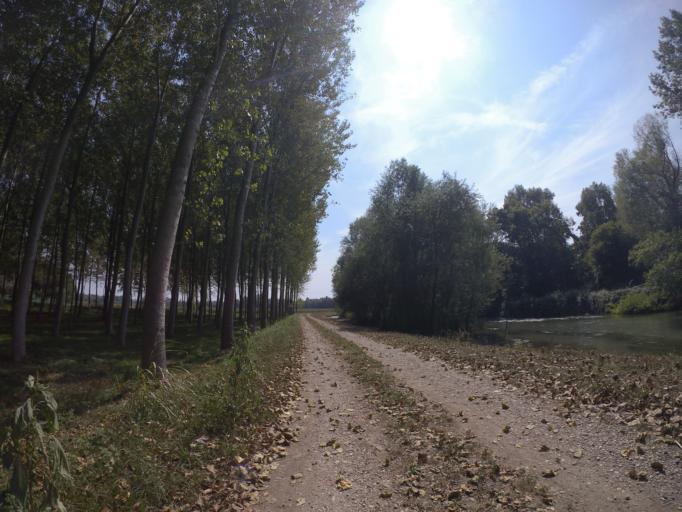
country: IT
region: Friuli Venezia Giulia
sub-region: Provincia di Udine
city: Varmo
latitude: 45.9105
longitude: 13.0189
